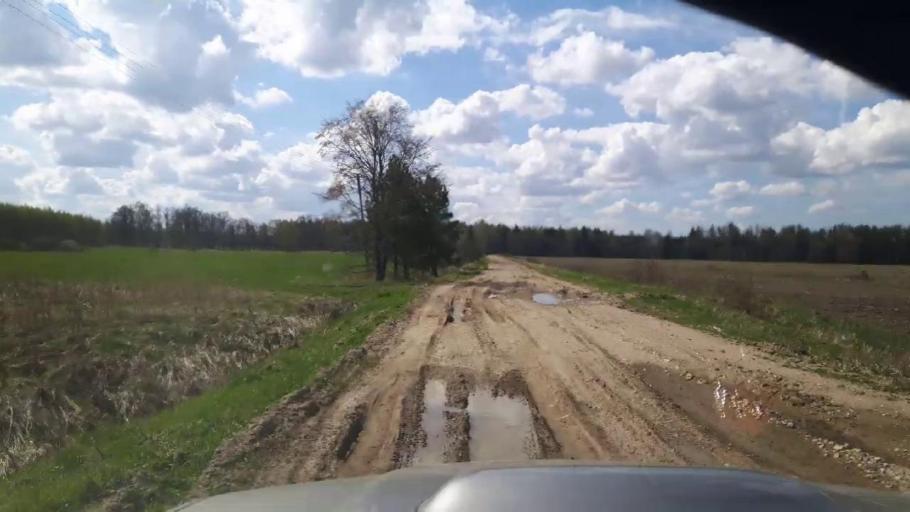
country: EE
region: Paernumaa
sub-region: Vaendra vald (alev)
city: Vandra
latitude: 58.5400
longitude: 25.0688
